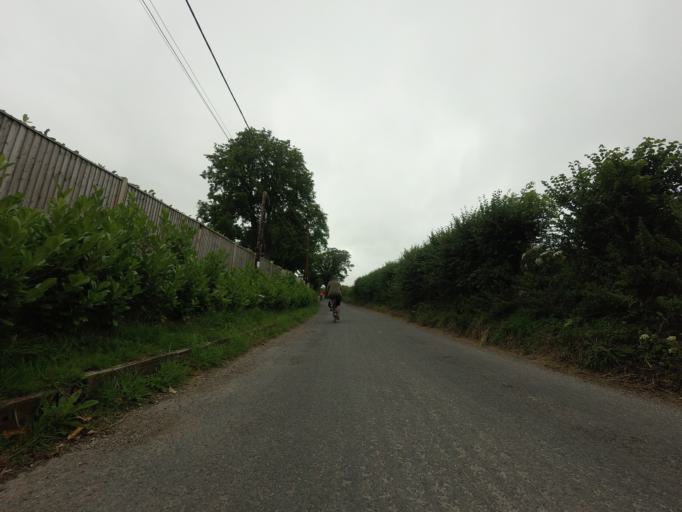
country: GB
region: England
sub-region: Kent
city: Borough Green
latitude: 51.3072
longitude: 0.2742
